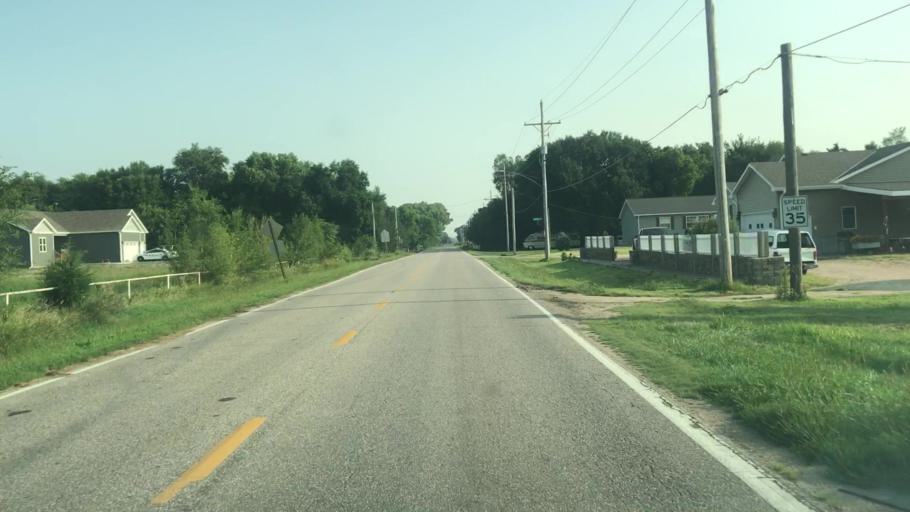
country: US
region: Nebraska
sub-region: Hall County
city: Grand Island
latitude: 40.9303
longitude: -98.3015
